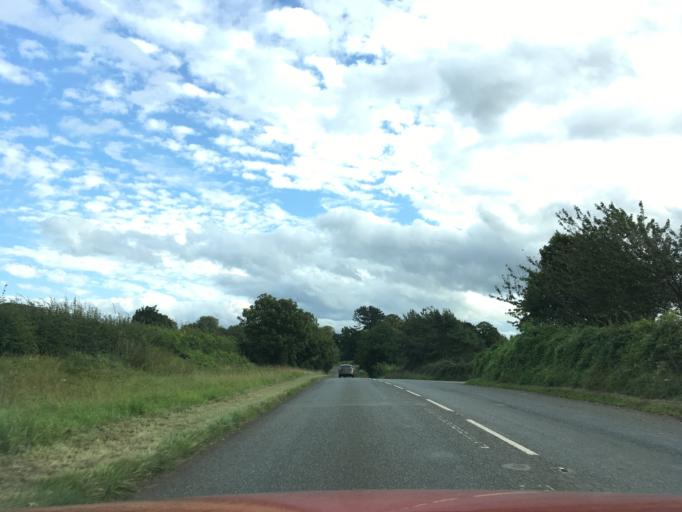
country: GB
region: England
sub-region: South Gloucestershire
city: Wickwar
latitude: 51.5993
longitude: -2.4060
